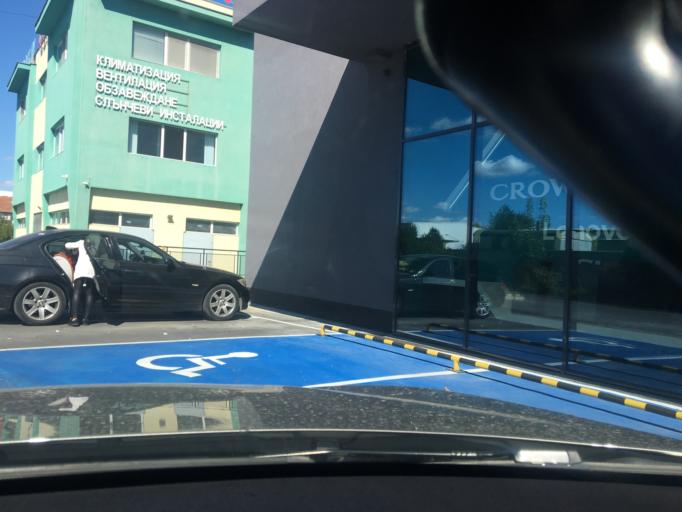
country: BG
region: Burgas
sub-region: Obshtina Burgas
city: Burgas
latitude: 42.5296
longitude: 27.4564
